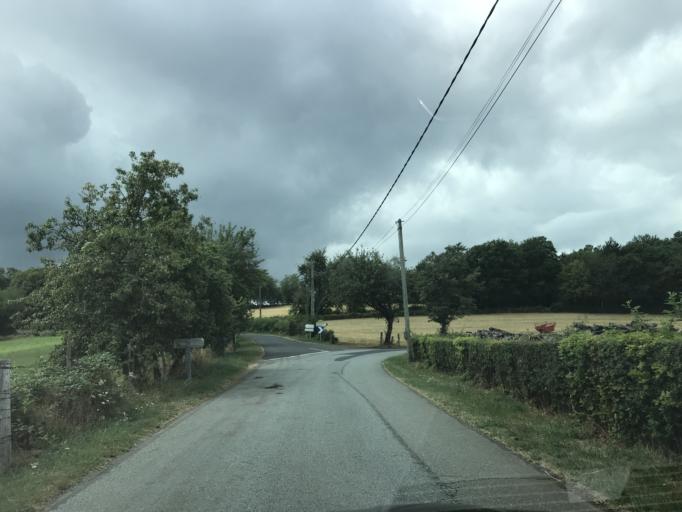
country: FR
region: Auvergne
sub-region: Departement du Cantal
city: Pleaux
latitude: 45.2403
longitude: 2.1940
